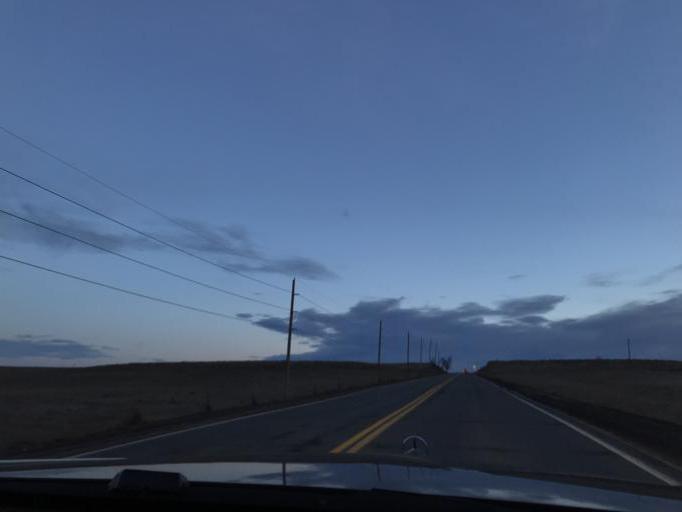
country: US
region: Colorado
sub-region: Boulder County
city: Superior
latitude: 39.8826
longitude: -105.1654
